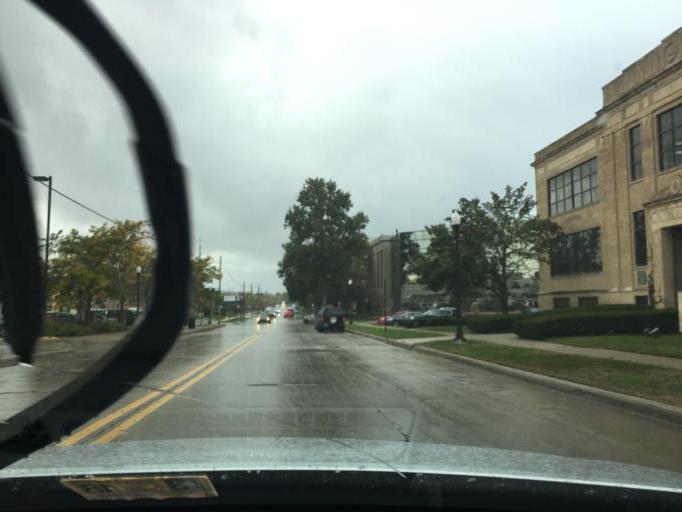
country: US
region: Michigan
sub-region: Wayne County
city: Dearborn Heights
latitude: 42.3073
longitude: -83.2445
